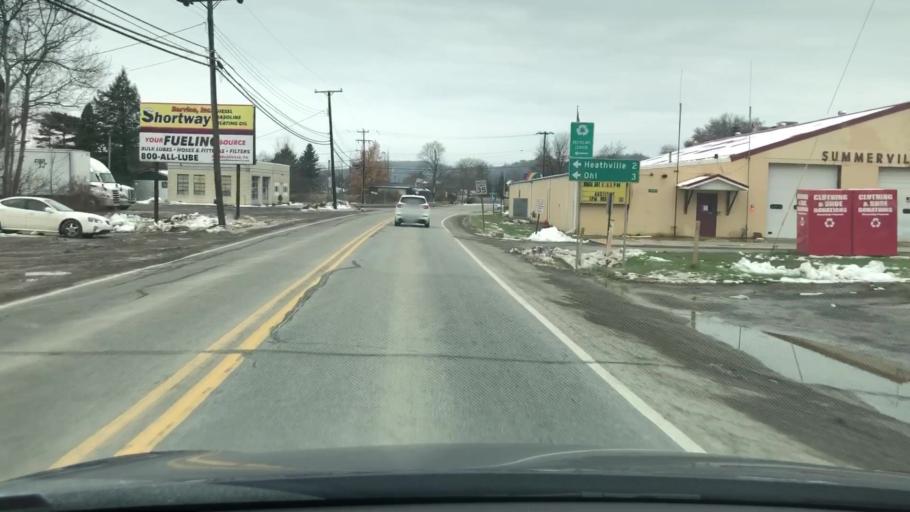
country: US
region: Pennsylvania
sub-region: Jefferson County
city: Brookville
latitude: 41.1207
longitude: -79.1861
